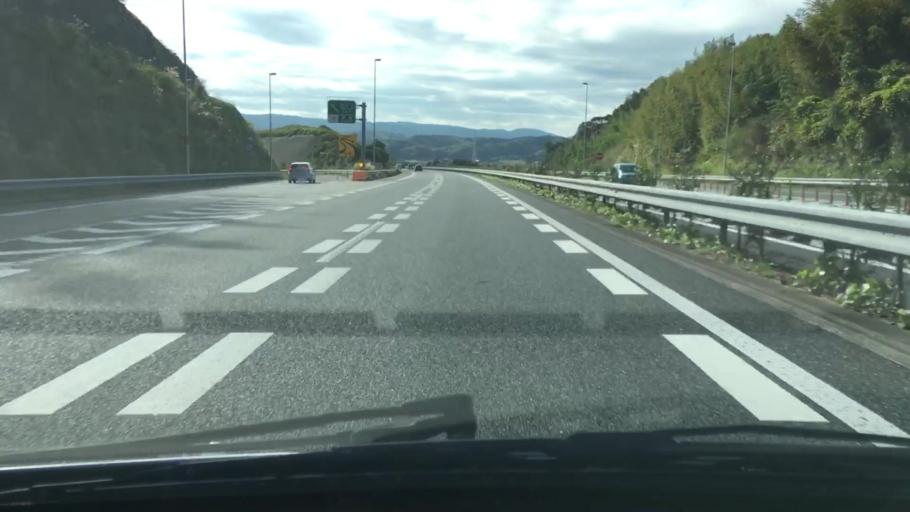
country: JP
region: Chiba
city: Kimitsu
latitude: 35.3217
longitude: 139.9448
